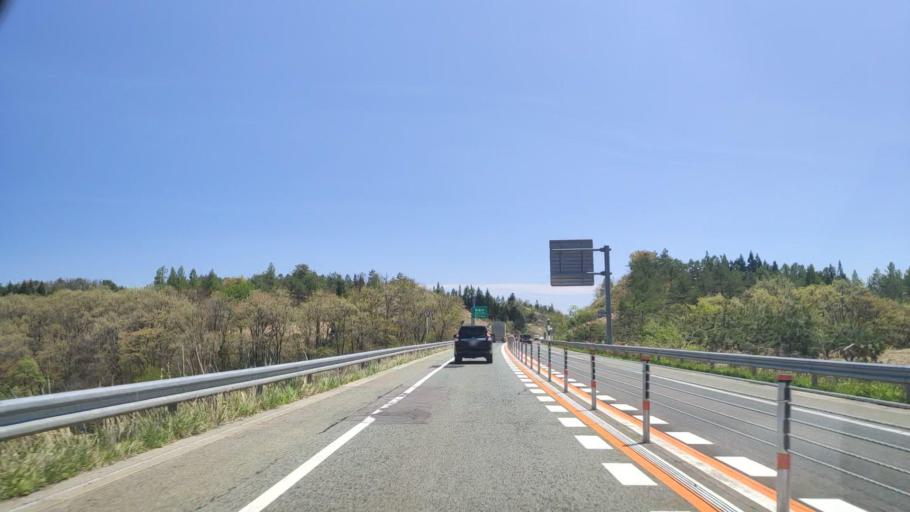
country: JP
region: Yamagata
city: Obanazawa
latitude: 38.6483
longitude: 140.3719
